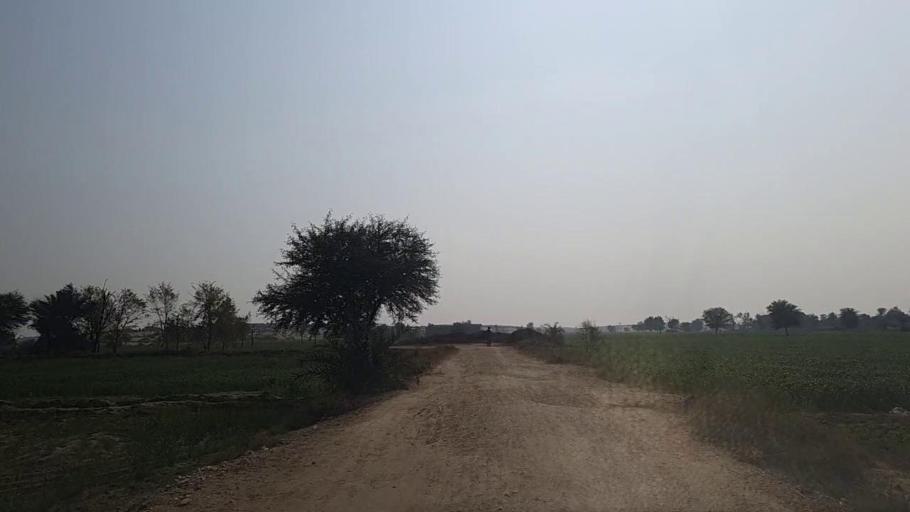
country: PK
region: Sindh
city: Jam Sahib
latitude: 26.4356
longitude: 68.5331
